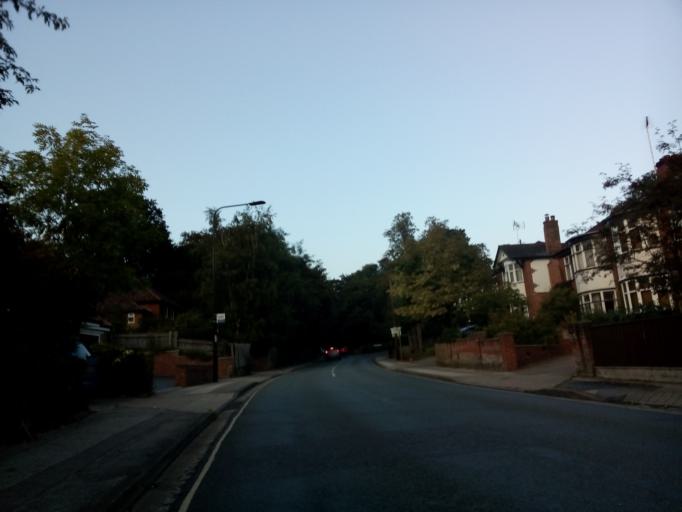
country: GB
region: England
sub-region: Suffolk
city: Ipswich
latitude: 52.0662
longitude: 1.1655
